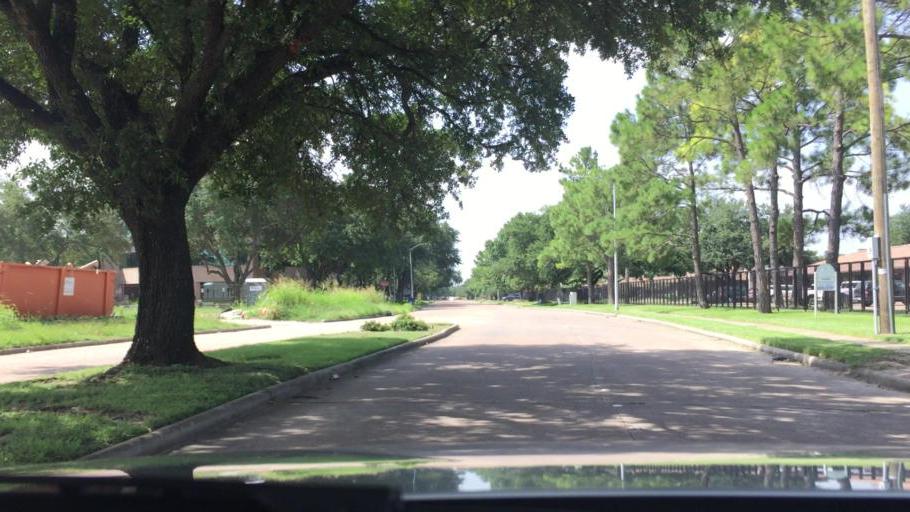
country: US
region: Texas
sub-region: Harris County
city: Hudson
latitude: 29.8503
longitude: -95.4949
